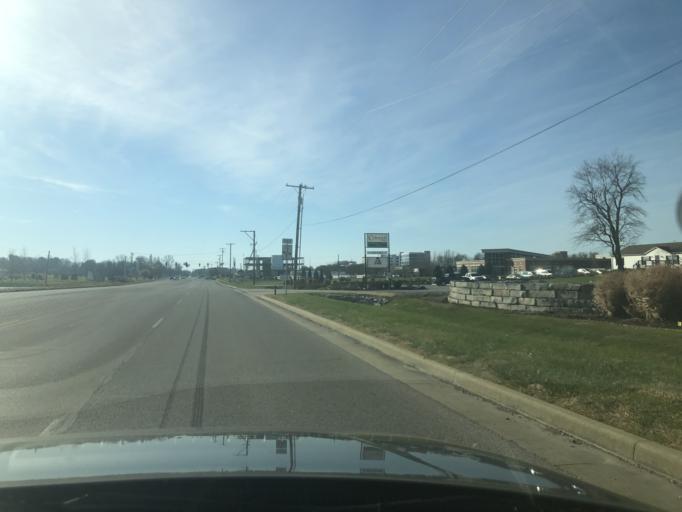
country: US
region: Indiana
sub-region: Warrick County
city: Newburgh
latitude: 37.9827
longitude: -87.4413
